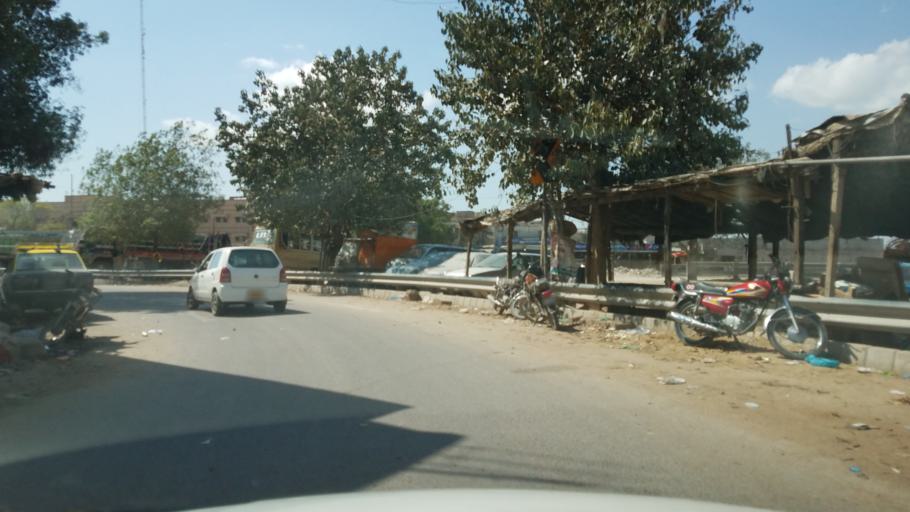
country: PK
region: Sindh
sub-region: Karachi District
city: Karachi
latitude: 24.9448
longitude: 67.0867
